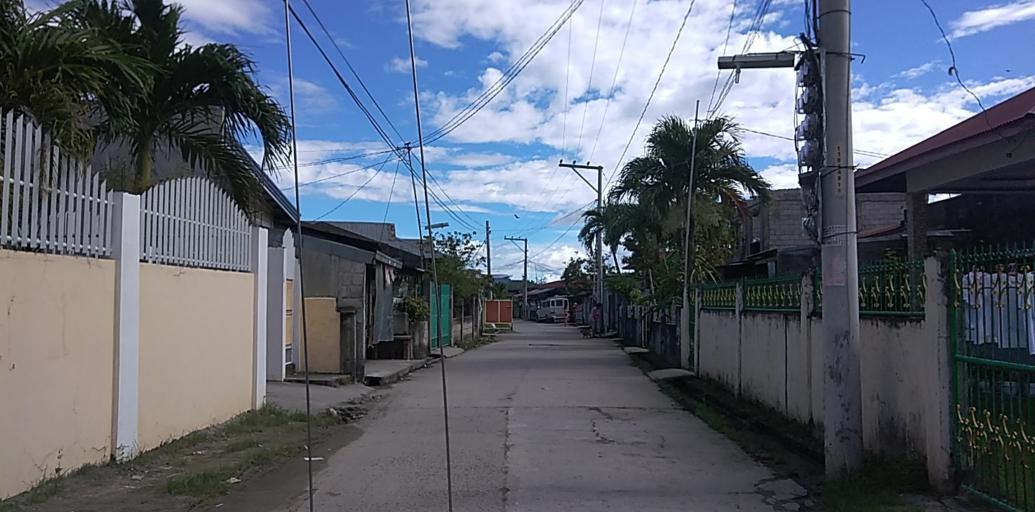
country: PH
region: Central Luzon
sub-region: Province of Pampanga
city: Candating
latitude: 15.1367
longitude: 120.8031
